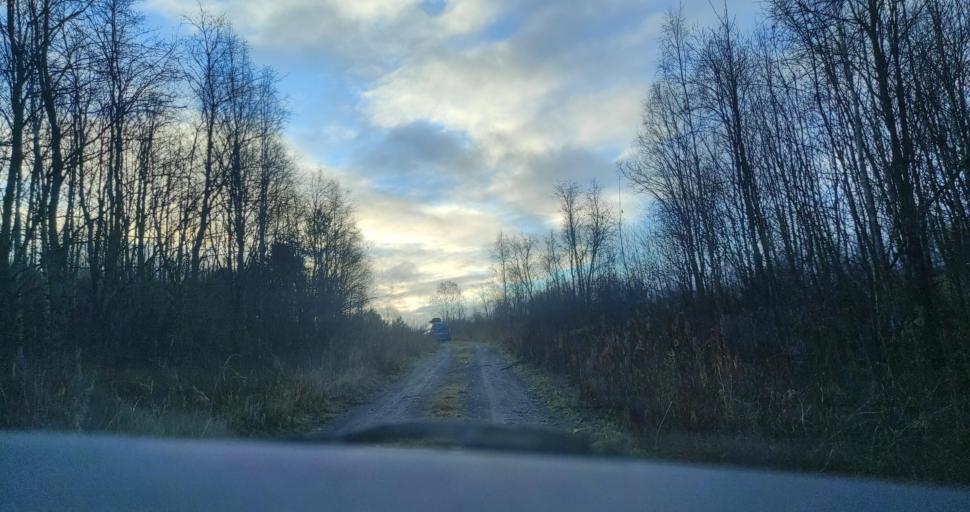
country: RU
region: Republic of Karelia
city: Pitkyaranta
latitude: 61.7298
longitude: 31.3802
